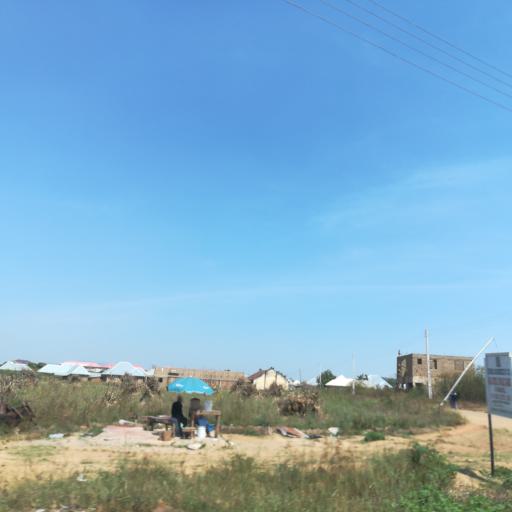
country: NG
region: Plateau
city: Jos
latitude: 9.8611
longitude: 8.9296
